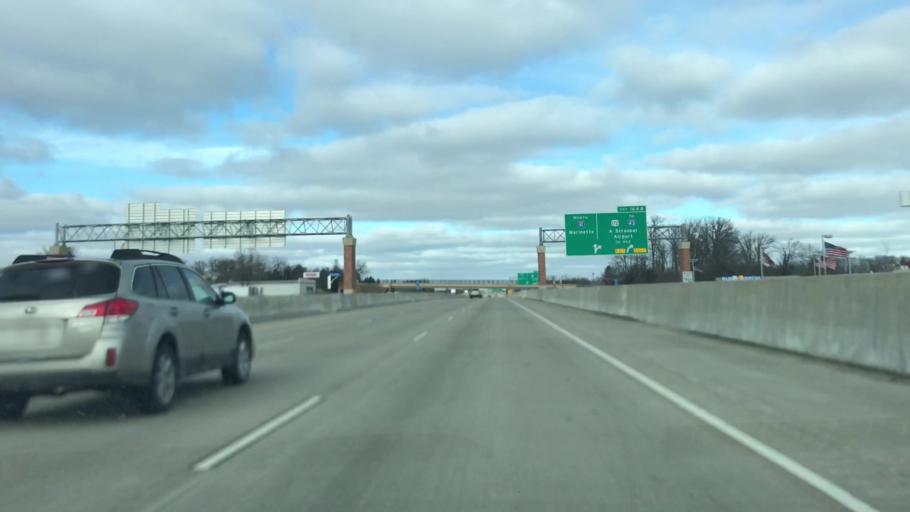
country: US
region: Wisconsin
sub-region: Brown County
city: Ashwaubenon
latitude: 44.4735
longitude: -88.0792
